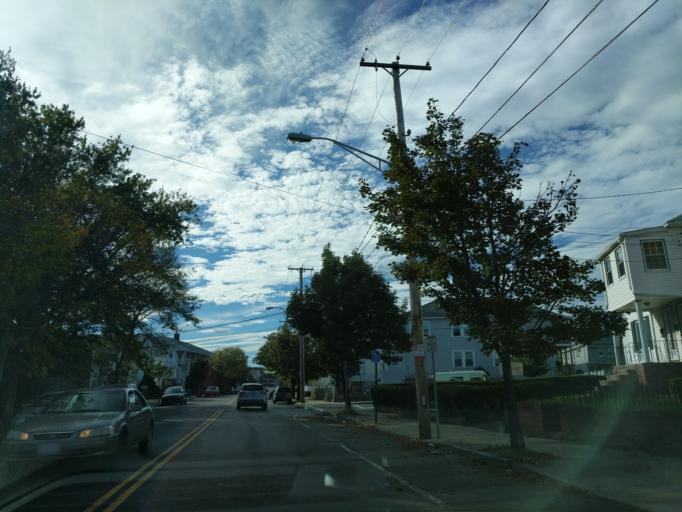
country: US
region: Massachusetts
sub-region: Middlesex County
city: Everett
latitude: 42.4029
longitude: -71.0427
